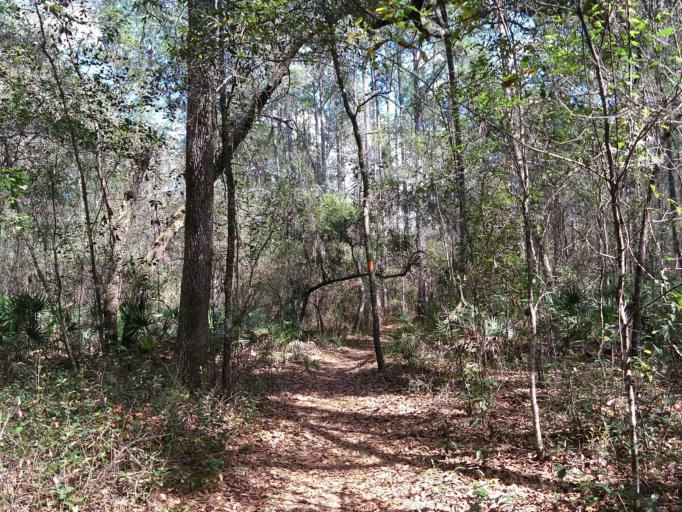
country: US
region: Florida
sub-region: Putnam County
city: Interlachen
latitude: 29.7652
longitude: -81.8431
